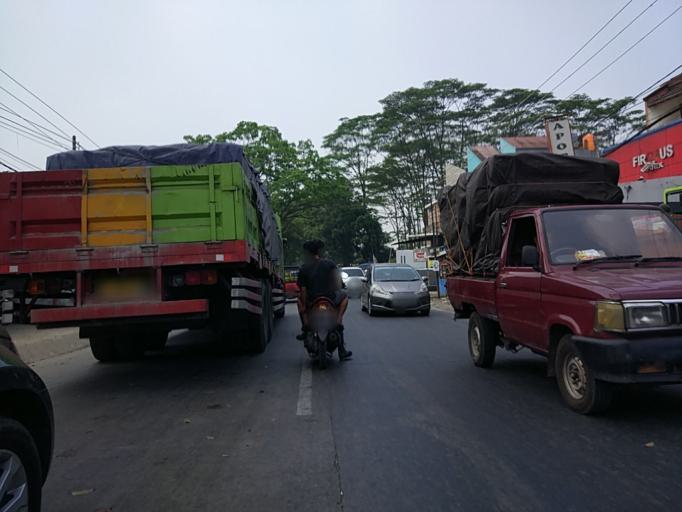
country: ID
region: West Java
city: Padalarang
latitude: -6.8390
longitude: 107.4767
